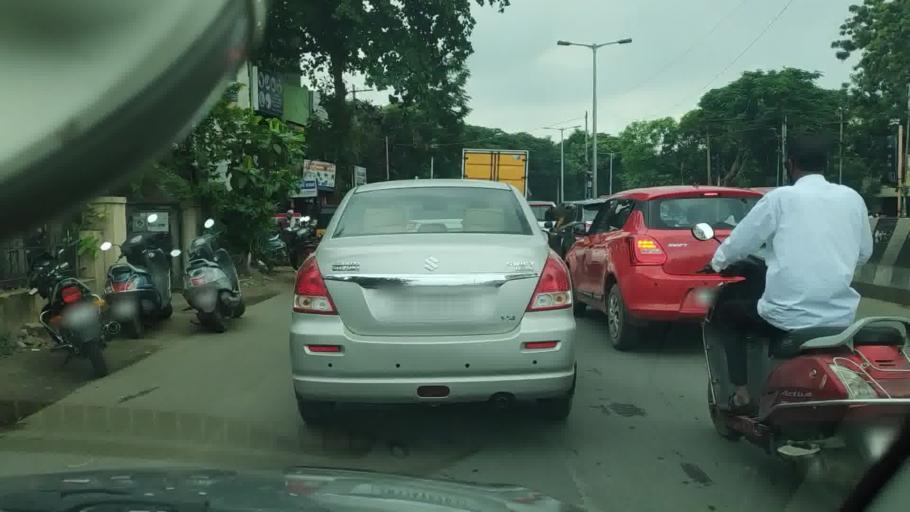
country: IN
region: Tamil Nadu
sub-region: Thiruvallur
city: Ambattur
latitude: 13.1182
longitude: 80.1497
